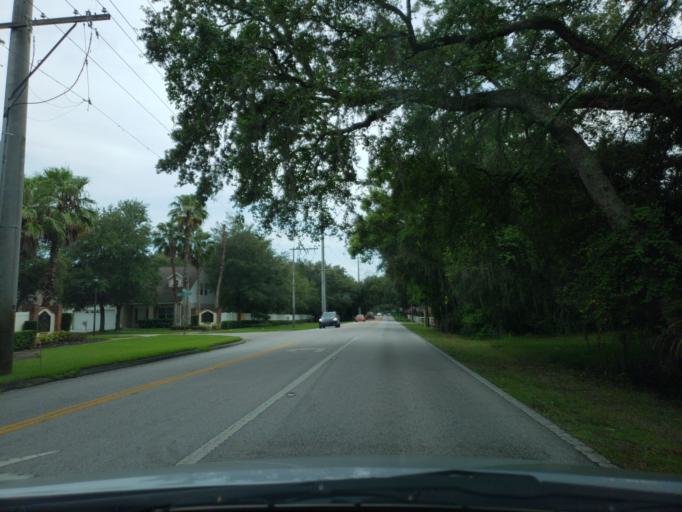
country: US
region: Florida
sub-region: Hillsborough County
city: University
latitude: 28.0956
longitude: -82.4307
